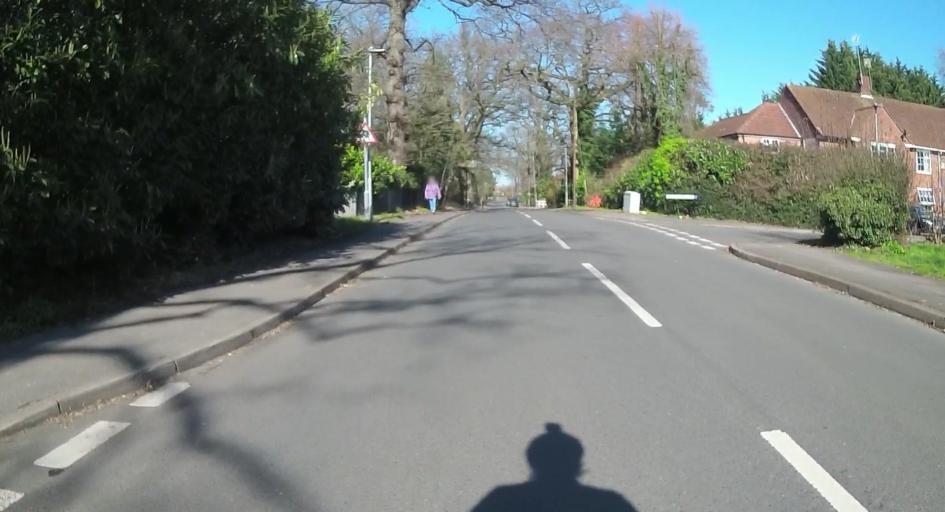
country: GB
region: England
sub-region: Bracknell Forest
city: Bracknell
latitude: 51.4203
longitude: -0.7623
